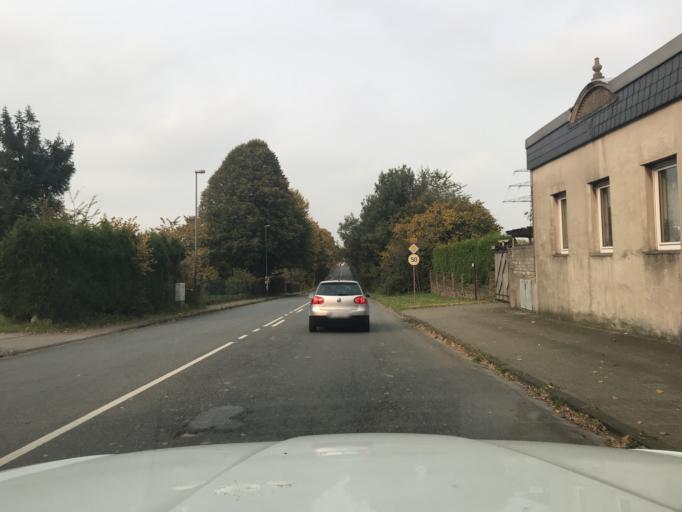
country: DE
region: North Rhine-Westphalia
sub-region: Regierungsbezirk Dusseldorf
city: Velbert
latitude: 51.3676
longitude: 7.0168
